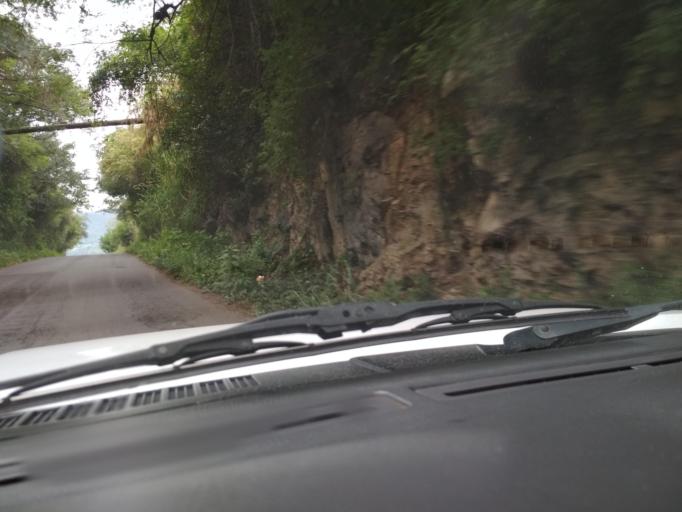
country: MX
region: Veracruz
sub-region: Actopan
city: Trapiche del Rosario
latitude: 19.5857
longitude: -96.7892
